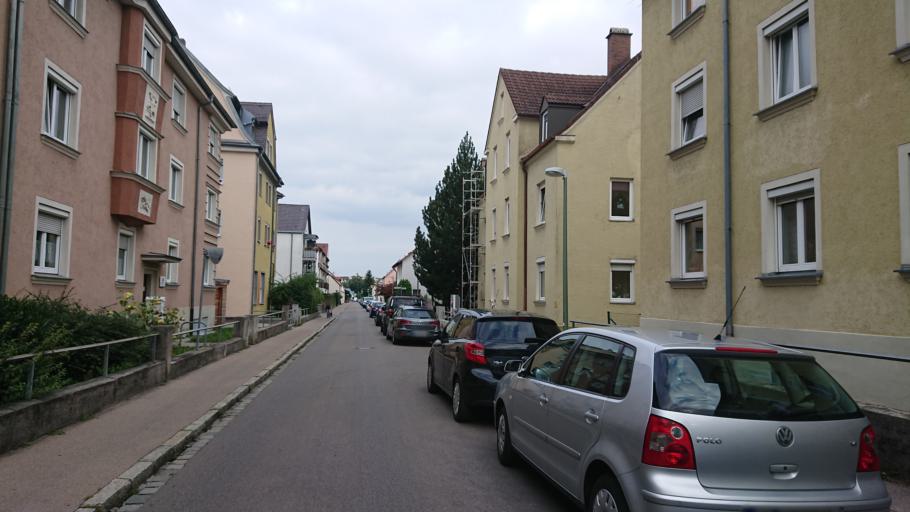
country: DE
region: Bavaria
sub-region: Swabia
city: Stadtbergen
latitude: 48.3643
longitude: 10.8654
